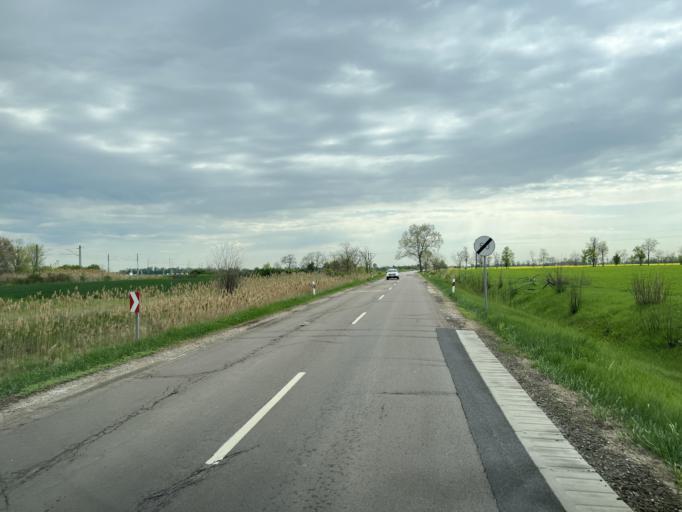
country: HU
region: Pest
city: Tortel
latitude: 47.1823
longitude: 19.8900
